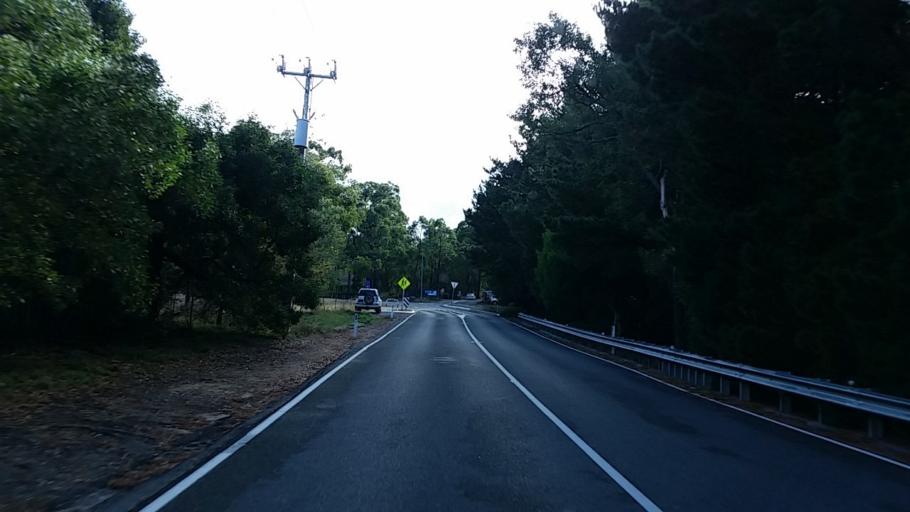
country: AU
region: South Australia
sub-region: Adelaide Hills
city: Crafers
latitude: -34.9777
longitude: 138.7094
